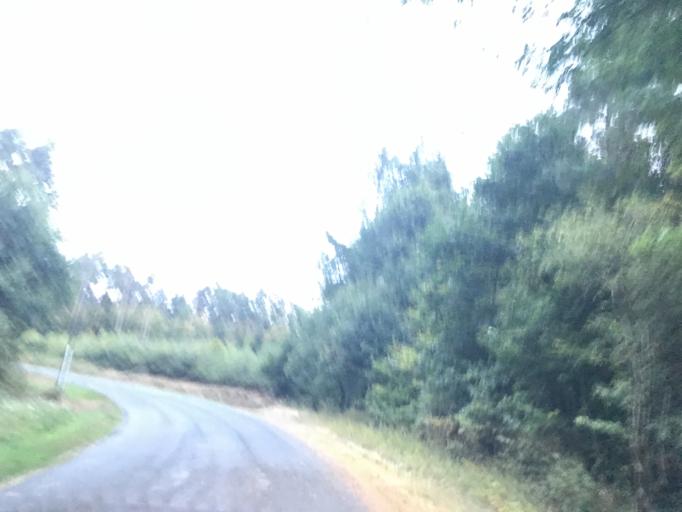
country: FR
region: Auvergne
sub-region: Departement du Puy-de-Dome
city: Escoutoux
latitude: 45.7998
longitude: 3.5671
